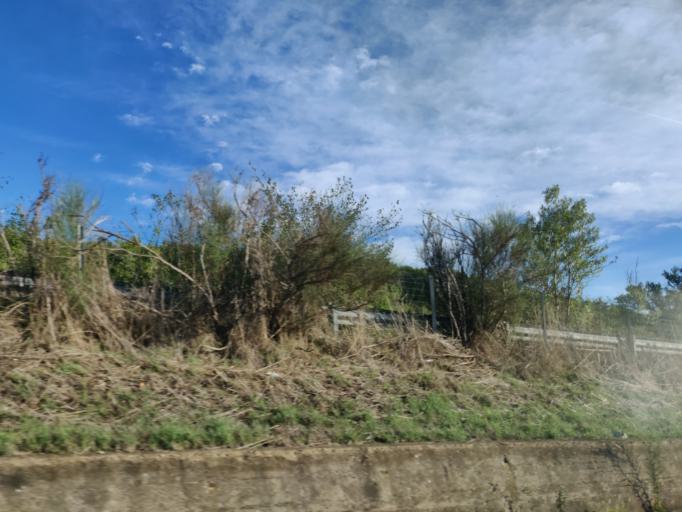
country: IT
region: Tuscany
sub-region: Provincia di Grosseto
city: Gavorrano
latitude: 42.9203
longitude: 10.9730
